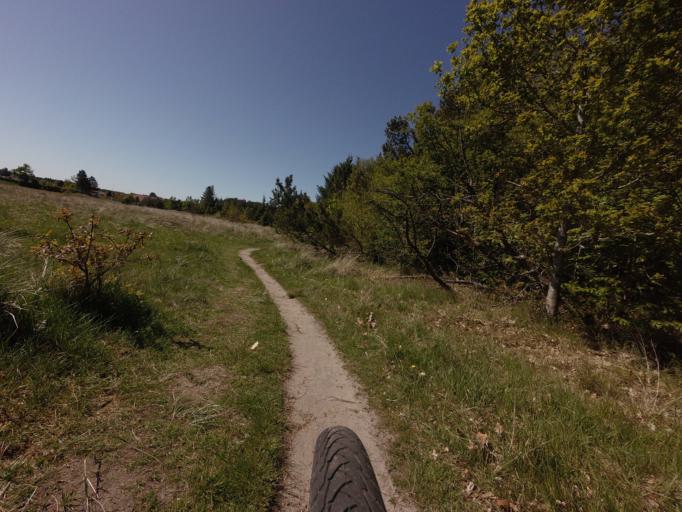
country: DK
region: North Denmark
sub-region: Jammerbugt Kommune
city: Pandrup
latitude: 57.2525
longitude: 9.6171
